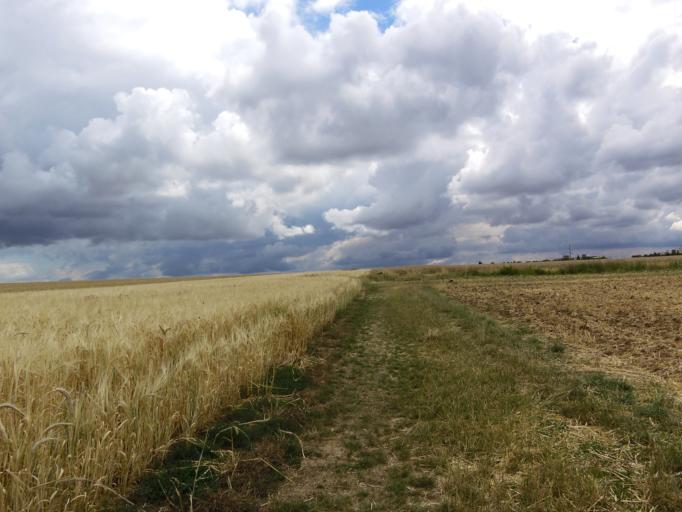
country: DE
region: Bavaria
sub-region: Regierungsbezirk Unterfranken
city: Estenfeld
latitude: 49.8183
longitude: 9.9742
